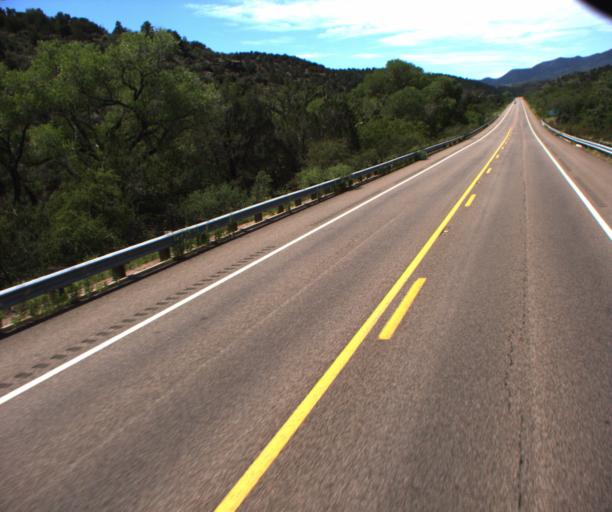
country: US
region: Arizona
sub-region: Gila County
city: Globe
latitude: 33.5754
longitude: -110.6560
